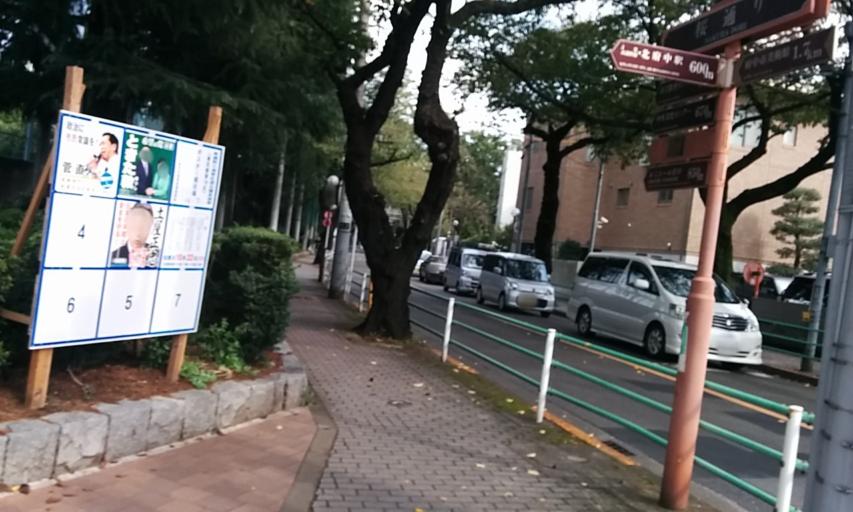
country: JP
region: Tokyo
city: Kokubunji
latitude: 35.6756
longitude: 139.4744
